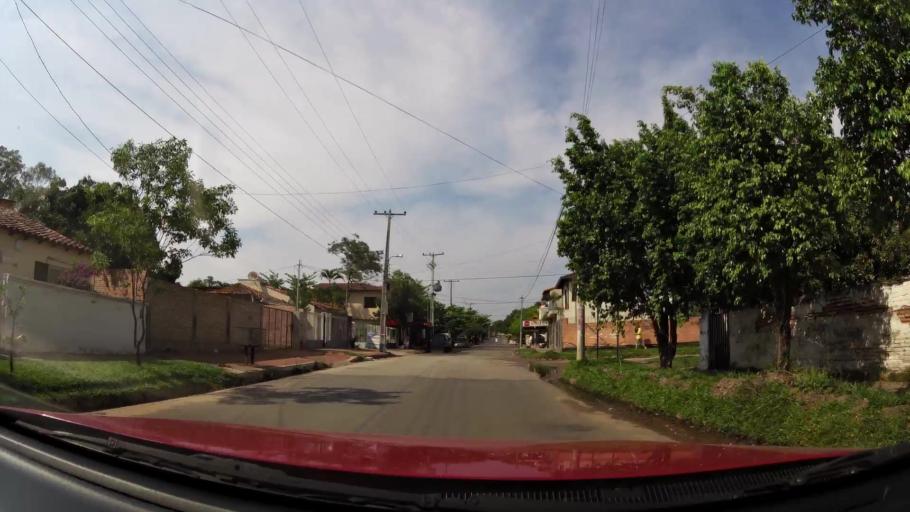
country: PY
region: Central
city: Fernando de la Mora
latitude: -25.2653
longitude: -57.5486
